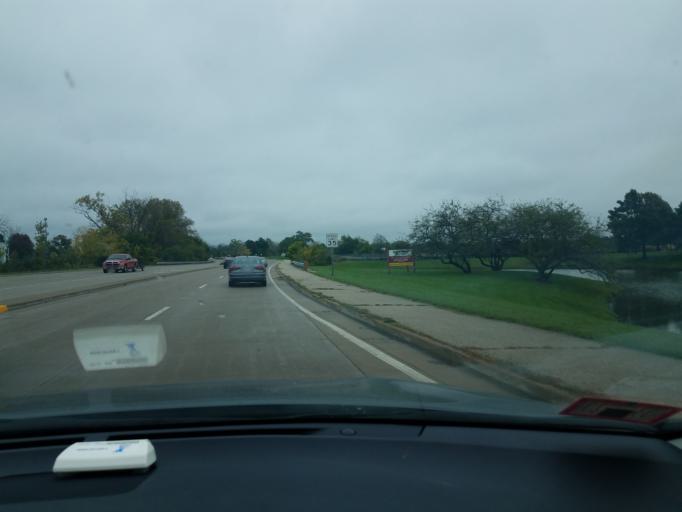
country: US
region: Illinois
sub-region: Lake County
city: Lincolnshire
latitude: 42.1974
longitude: -87.9368
